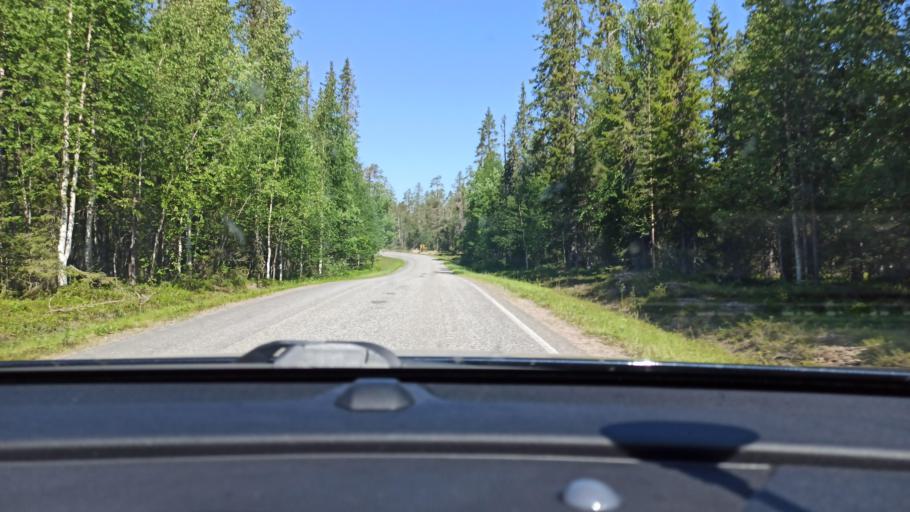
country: FI
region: Lapland
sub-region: Tunturi-Lappi
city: Kolari
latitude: 67.6674
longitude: 24.1596
